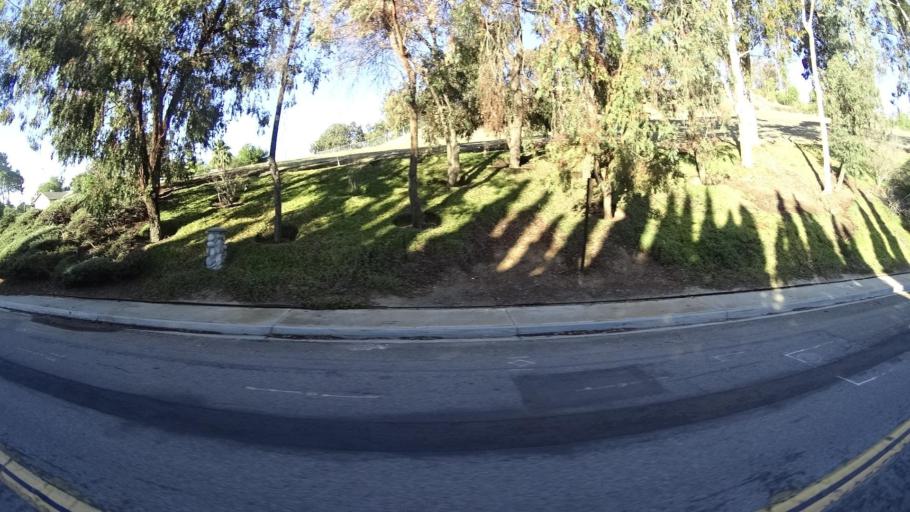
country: US
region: California
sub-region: San Diego County
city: Bonita
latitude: 32.6726
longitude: -117.0343
